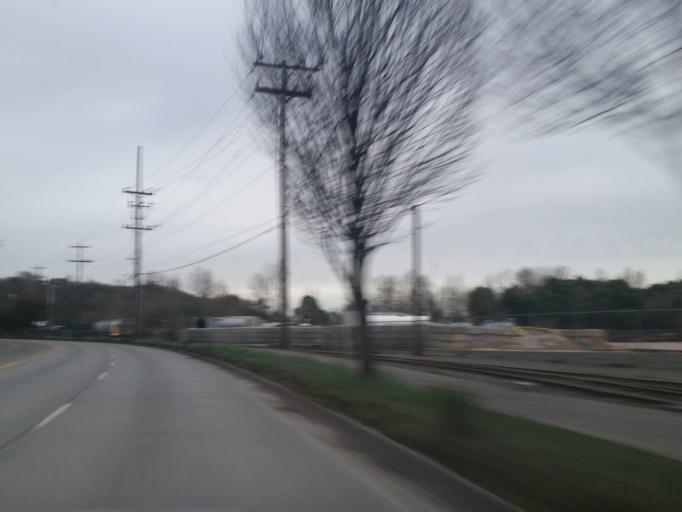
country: US
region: Washington
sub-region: King County
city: White Center
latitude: 47.5540
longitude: -122.3471
